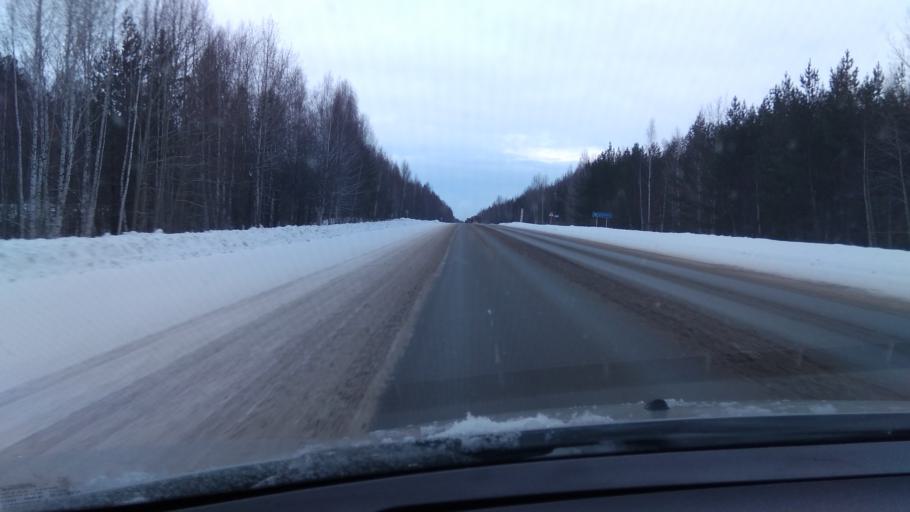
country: RU
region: Sverdlovsk
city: Tsementnyy
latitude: 57.4150
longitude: 60.2117
